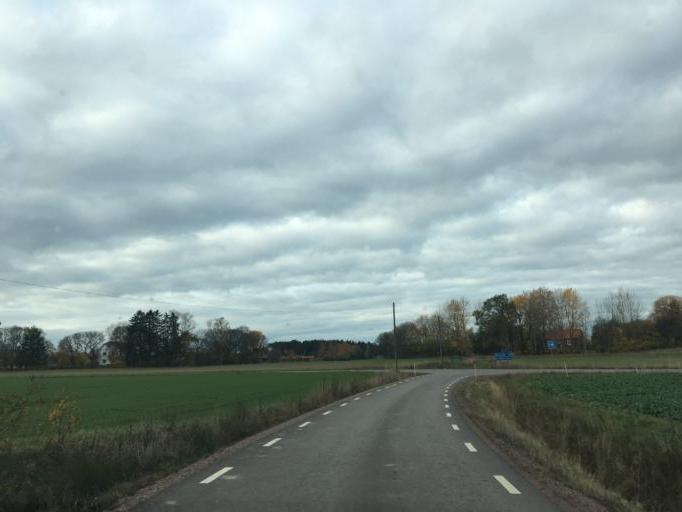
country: SE
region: Vaestmanland
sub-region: Vasteras
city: Vasteras
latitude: 59.5754
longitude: 16.4547
